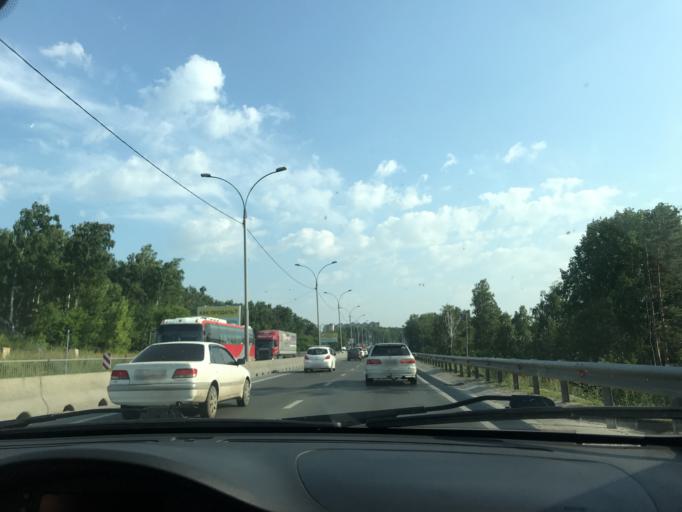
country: RU
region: Novosibirsk
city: Akademgorodok
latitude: 54.8138
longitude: 83.0891
